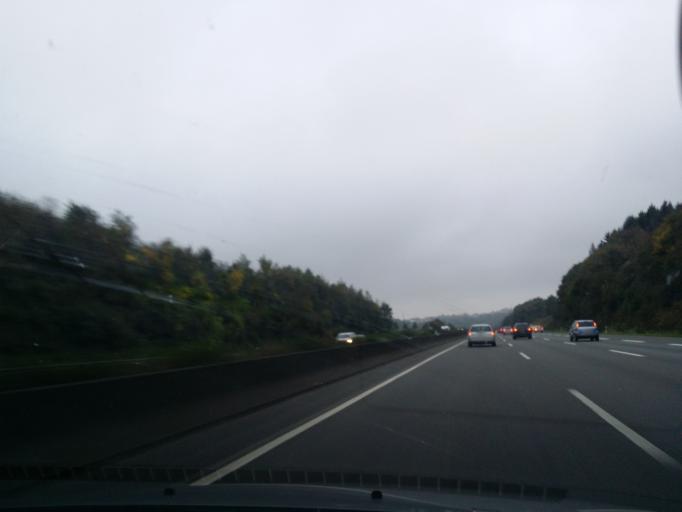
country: DE
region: North Rhine-Westphalia
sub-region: Regierungsbezirk Dusseldorf
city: Remscheid
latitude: 51.2026
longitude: 7.2481
